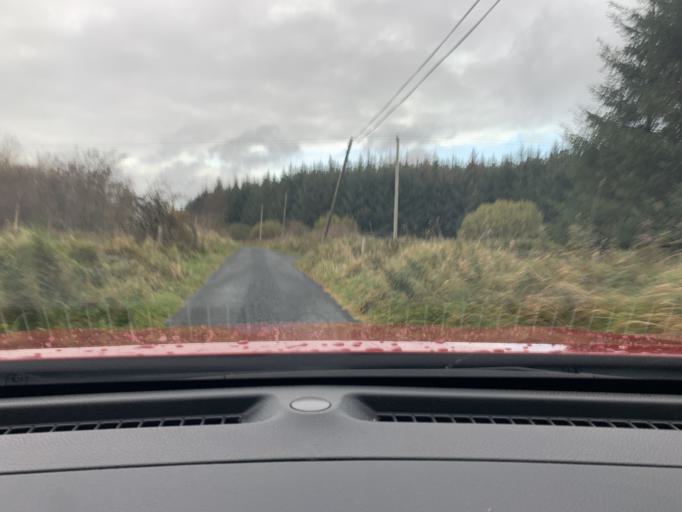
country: IE
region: Connaught
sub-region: Roscommon
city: Ballaghaderreen
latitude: 53.9730
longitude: -8.6000
